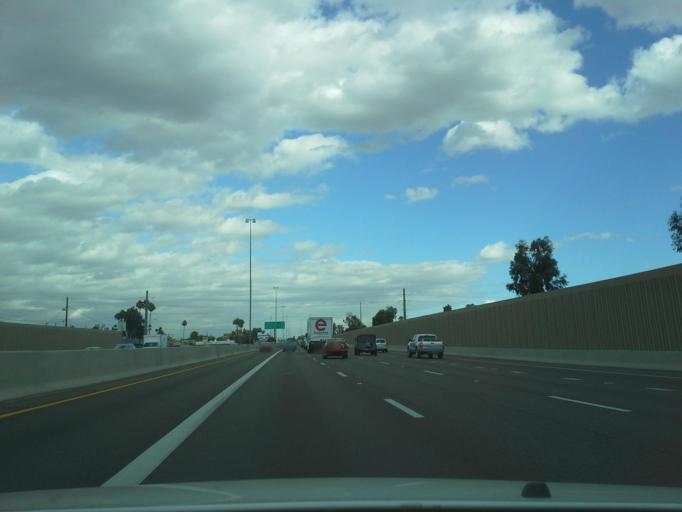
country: US
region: Arizona
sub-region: Maricopa County
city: Phoenix
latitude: 33.5003
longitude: -112.1129
